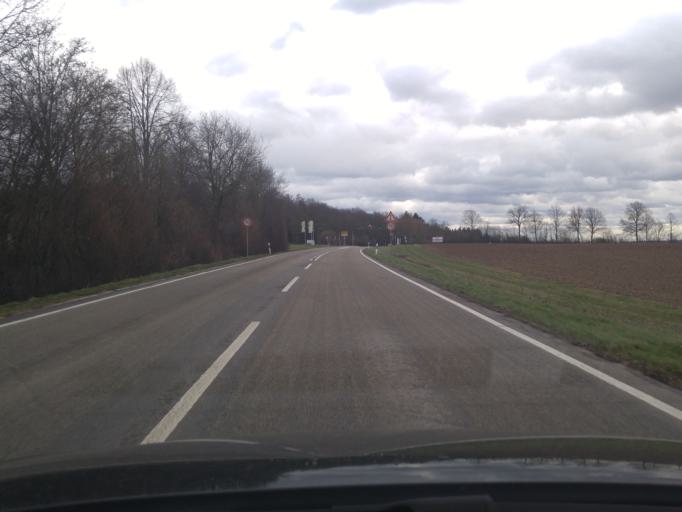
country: DE
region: Baden-Wuerttemberg
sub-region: Regierungsbezirk Stuttgart
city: Bad Rappenau
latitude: 49.2329
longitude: 9.1102
